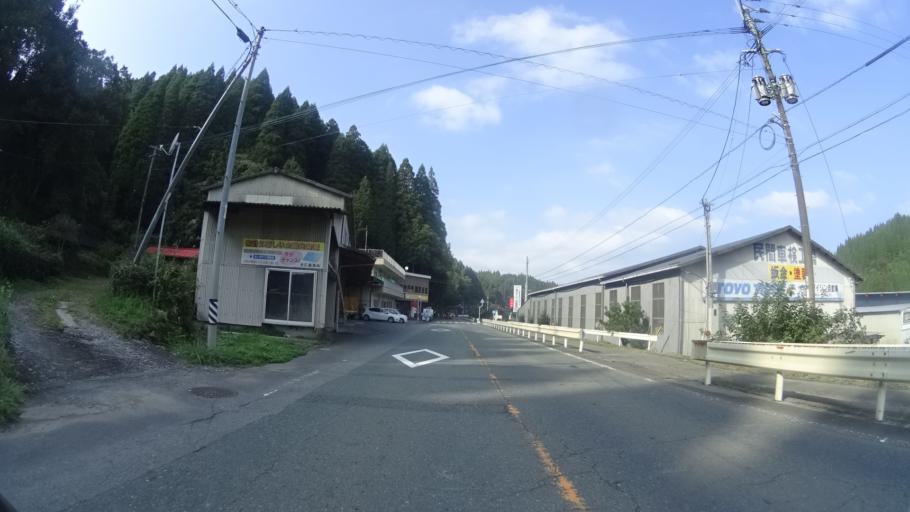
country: JP
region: Kumamoto
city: Aso
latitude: 33.0902
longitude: 131.0675
